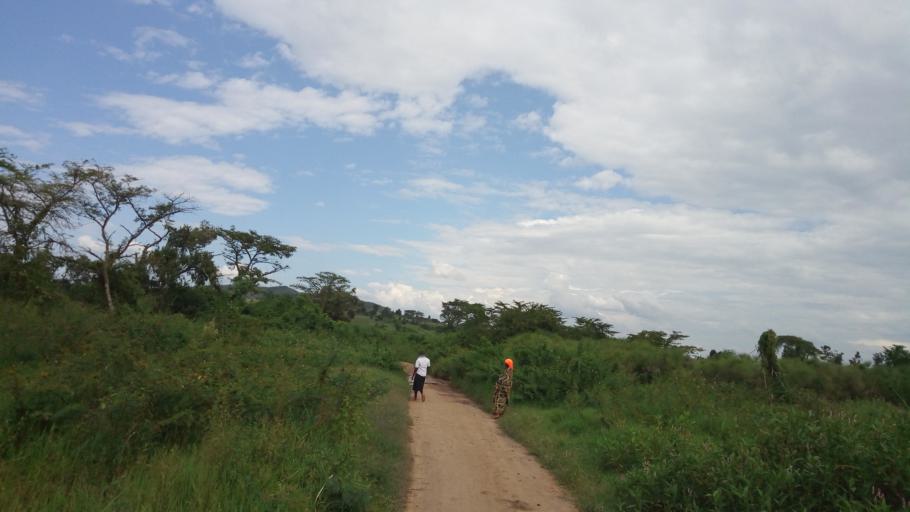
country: UG
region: Central Region
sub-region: Kiboga District
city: Kiboga
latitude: 0.7608
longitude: 31.6949
